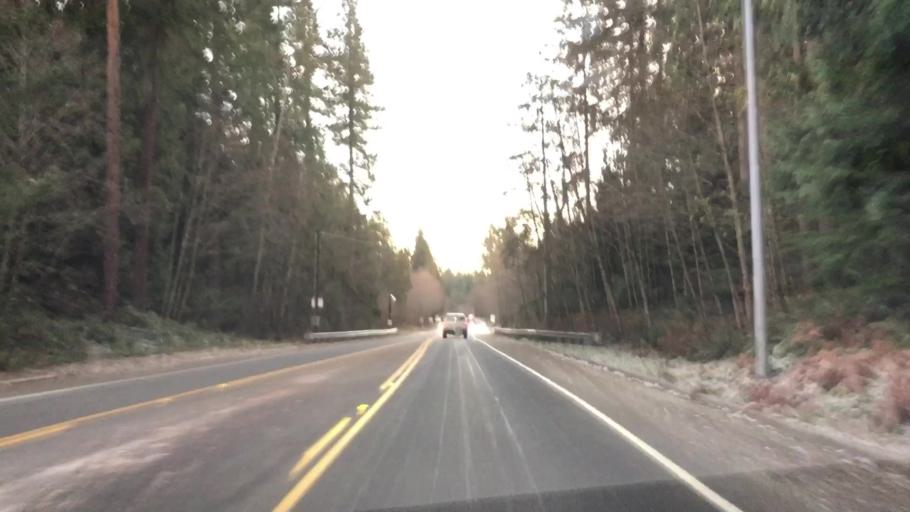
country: US
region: Washington
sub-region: King County
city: Union Hill-Novelty Hill
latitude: 47.7187
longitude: -122.0401
